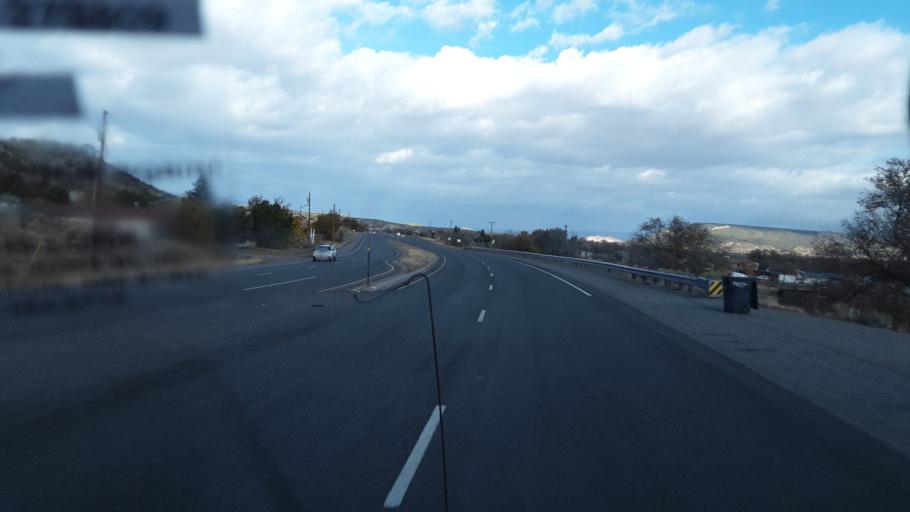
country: US
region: New Mexico
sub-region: Rio Arriba County
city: Ohkay Owingeh
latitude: 36.0360
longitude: -106.0952
